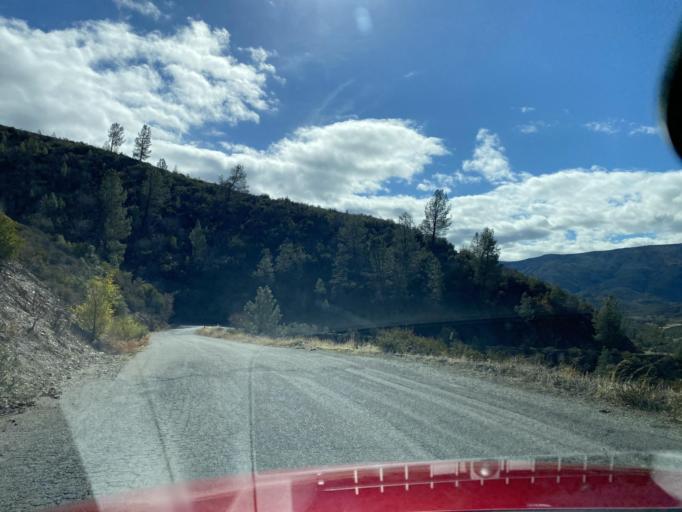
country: US
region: California
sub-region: Lake County
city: Lucerne
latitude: 39.3640
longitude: -122.6509
